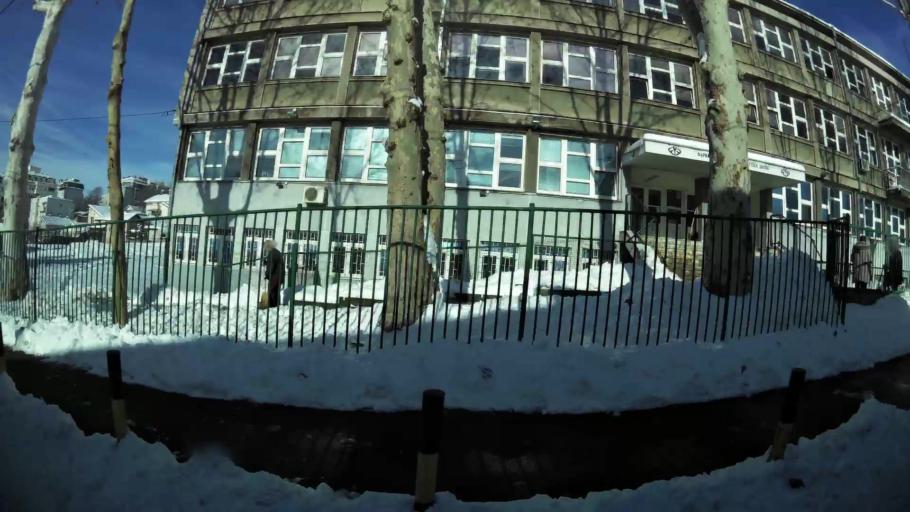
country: RS
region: Central Serbia
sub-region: Belgrade
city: Palilula
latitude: 44.7902
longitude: 20.5036
